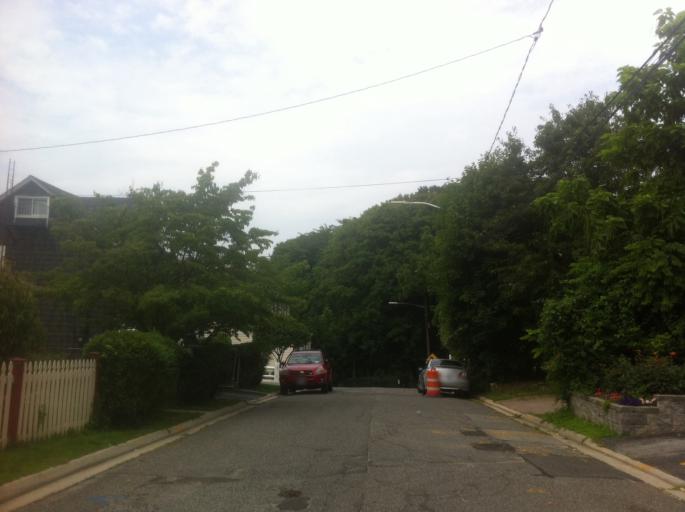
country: US
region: New York
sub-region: Nassau County
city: Locust Valley
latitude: 40.8770
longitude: -73.6093
